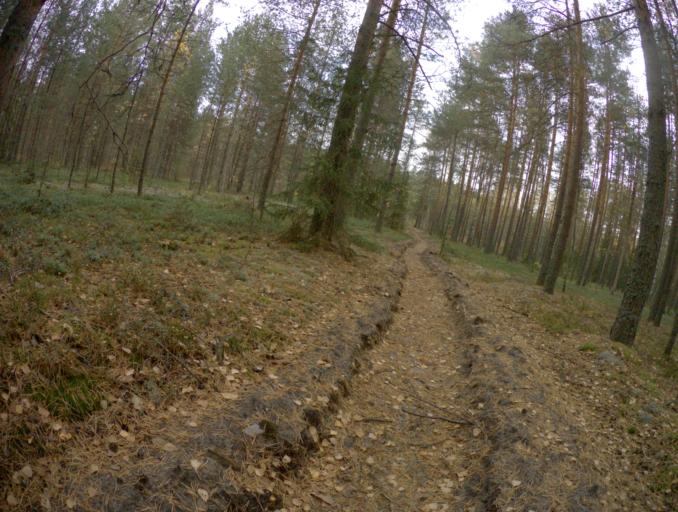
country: RU
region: Vladimir
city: Raduzhnyy
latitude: 55.9362
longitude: 40.3336
